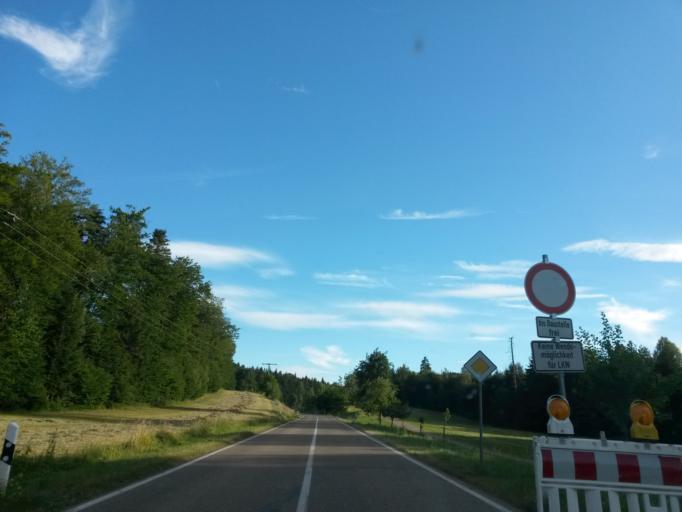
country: DE
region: Baden-Wuerttemberg
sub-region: Regierungsbezirk Stuttgart
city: Ellenberg
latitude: 49.0256
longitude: 10.2248
